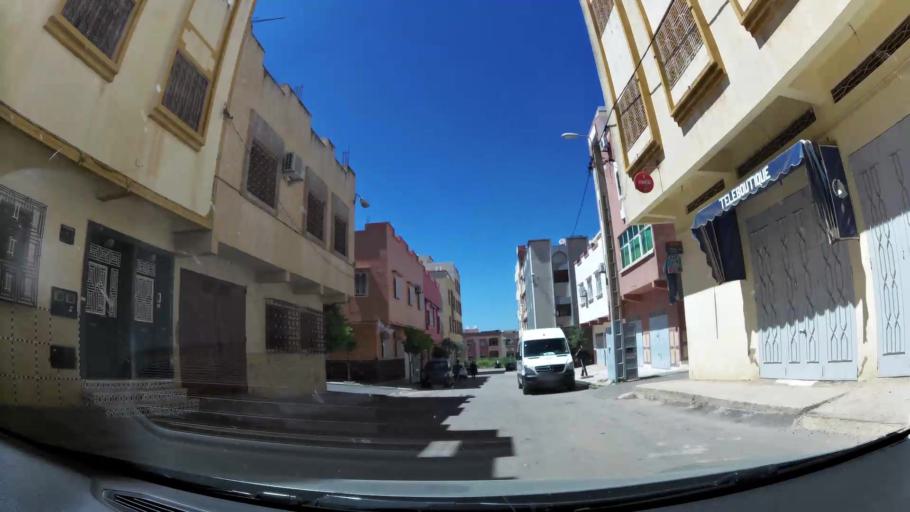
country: MA
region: Meknes-Tafilalet
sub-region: Meknes
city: Meknes
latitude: 33.8963
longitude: -5.5826
